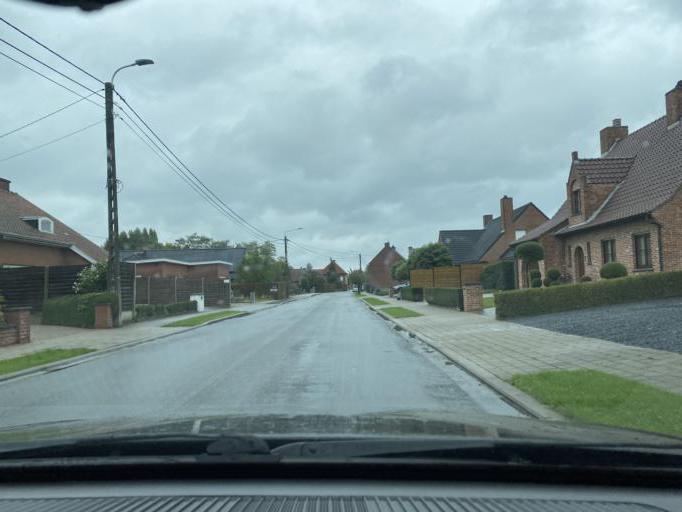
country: BE
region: Flanders
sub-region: Provincie West-Vlaanderen
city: Wielsbeke
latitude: 50.9160
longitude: 3.3996
